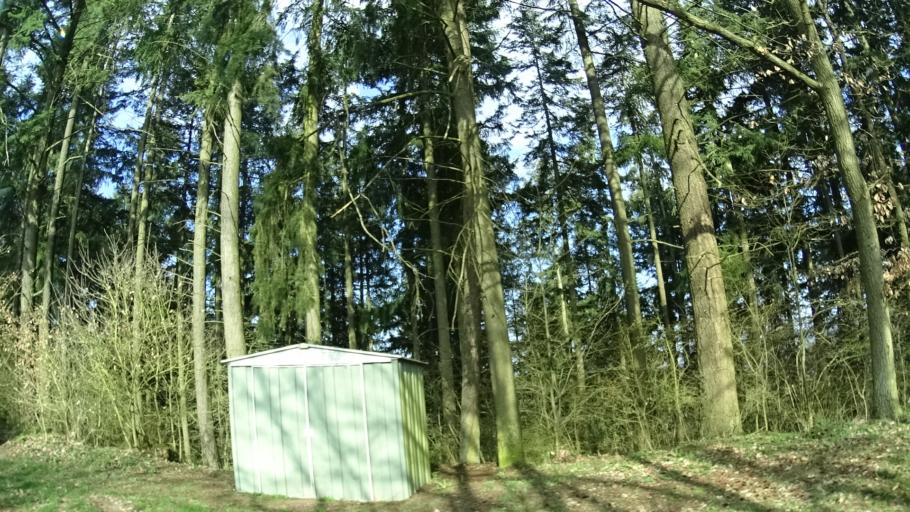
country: DE
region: Rheinland-Pfalz
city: Idar-Oberstein
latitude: 49.6882
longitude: 7.3242
